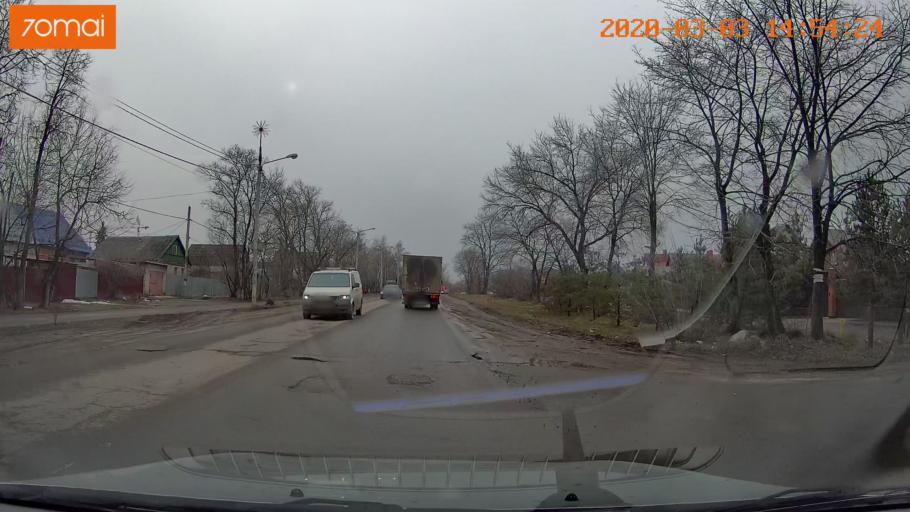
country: RU
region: Moskovskaya
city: Korenevo
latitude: 55.6713
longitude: 38.0032
